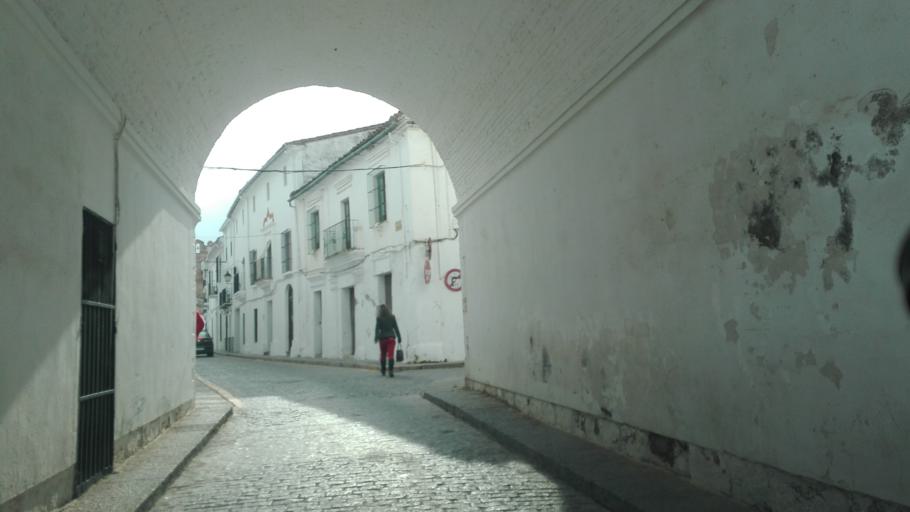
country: ES
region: Extremadura
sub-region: Provincia de Badajoz
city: Llerena
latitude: 38.2378
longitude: -6.0147
